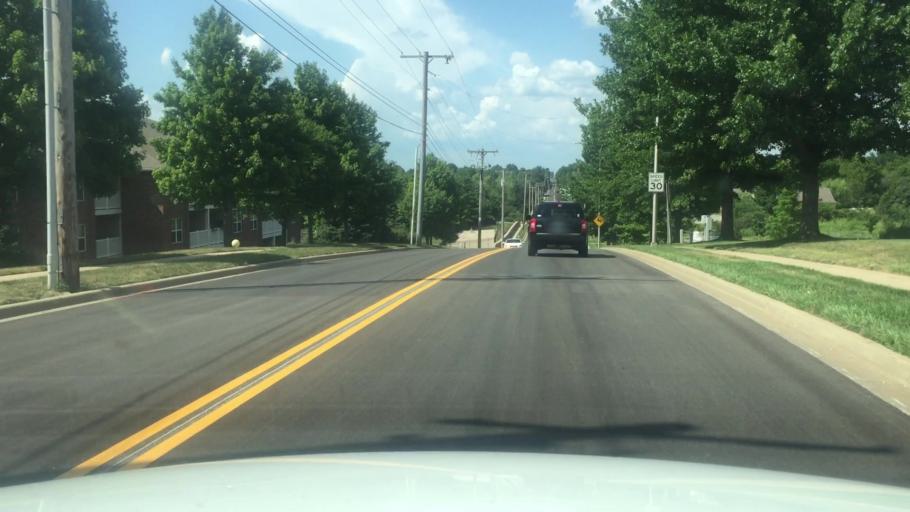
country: US
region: Kansas
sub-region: Johnson County
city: Lenexa
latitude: 38.9730
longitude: -94.7423
